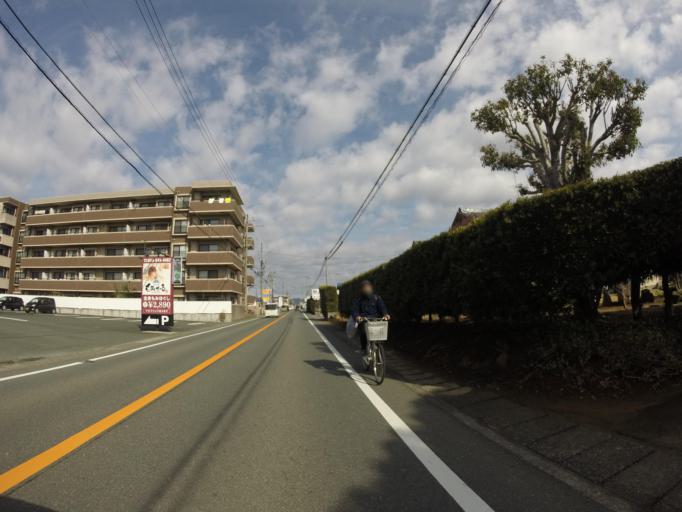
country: JP
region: Shizuoka
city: Hamakita
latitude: 34.7951
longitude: 137.7011
